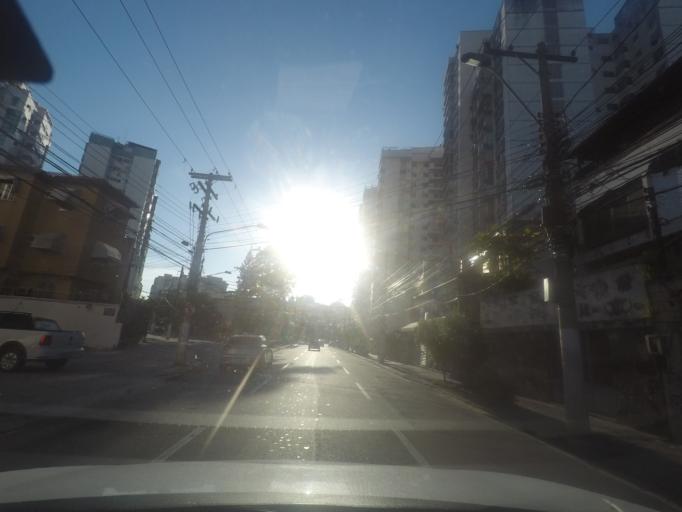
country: BR
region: Rio de Janeiro
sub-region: Niteroi
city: Niteroi
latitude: -22.8991
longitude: -43.1069
